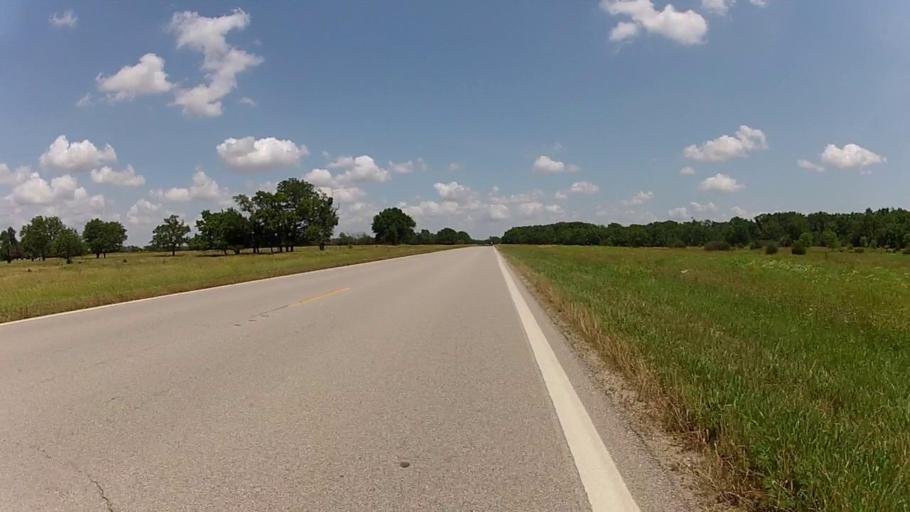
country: US
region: Kansas
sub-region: Labette County
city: Altamont
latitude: 37.1937
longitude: -95.3927
